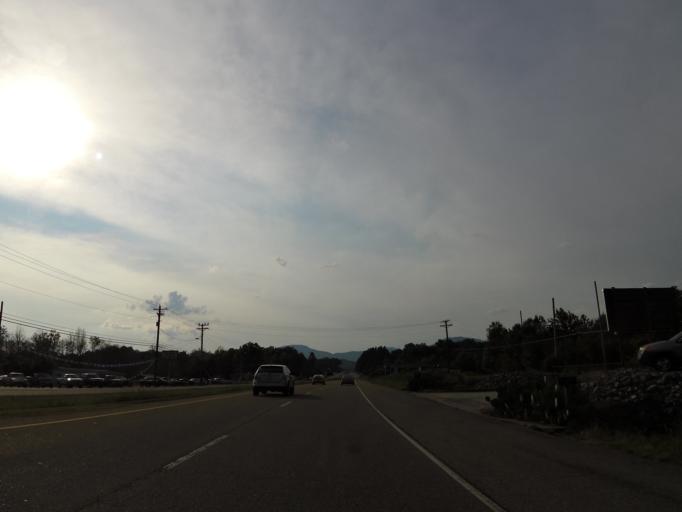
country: US
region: Tennessee
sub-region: Anderson County
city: Oak Ridge
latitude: 36.0191
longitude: -84.3078
